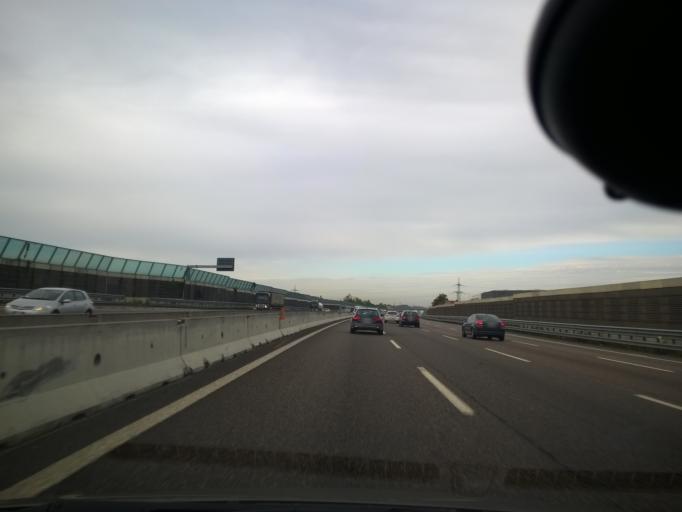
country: IT
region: Lombardy
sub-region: Provincia di Bergamo
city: Osio Sopra
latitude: 45.6226
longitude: 9.5809
